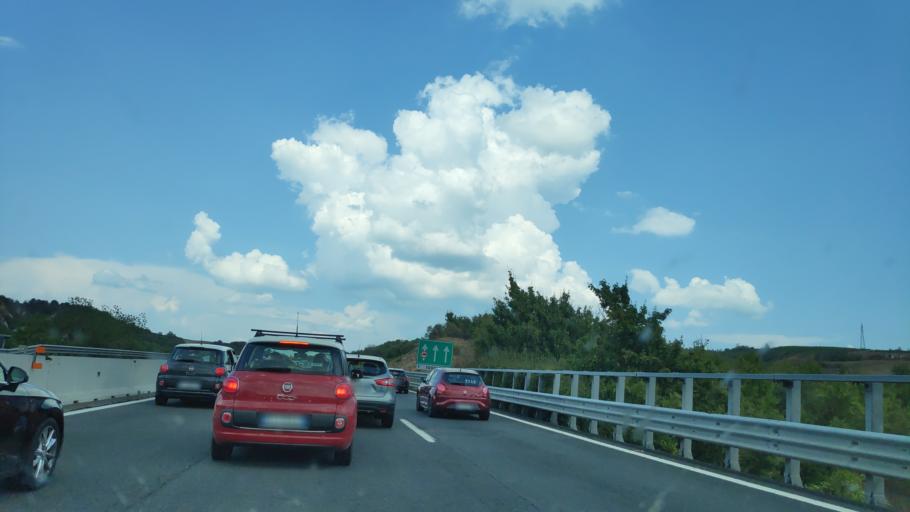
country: IT
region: Umbria
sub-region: Provincia di Terni
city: Ficulle
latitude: 42.8286
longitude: 12.0425
